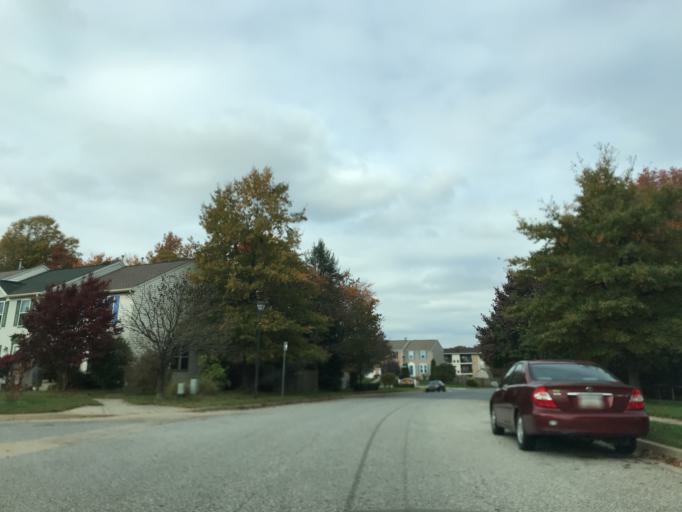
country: US
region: Maryland
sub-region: Baltimore County
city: Bowleys Quarters
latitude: 39.3266
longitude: -76.3923
